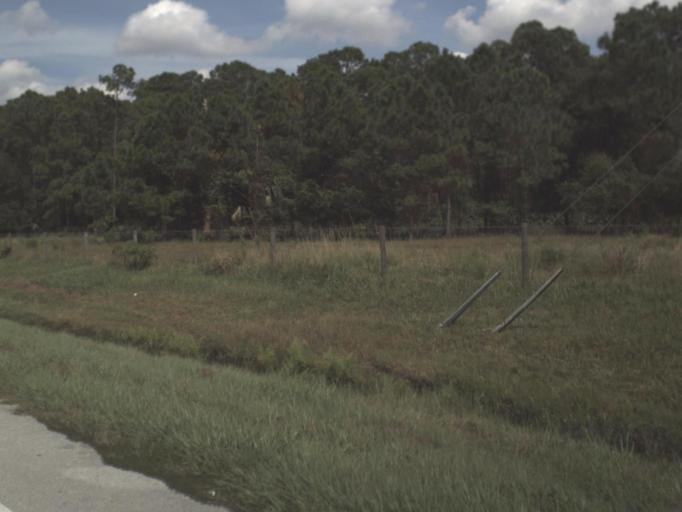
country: US
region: Florida
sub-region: Okeechobee County
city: Cypress Quarters
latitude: 27.3095
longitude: -80.8259
